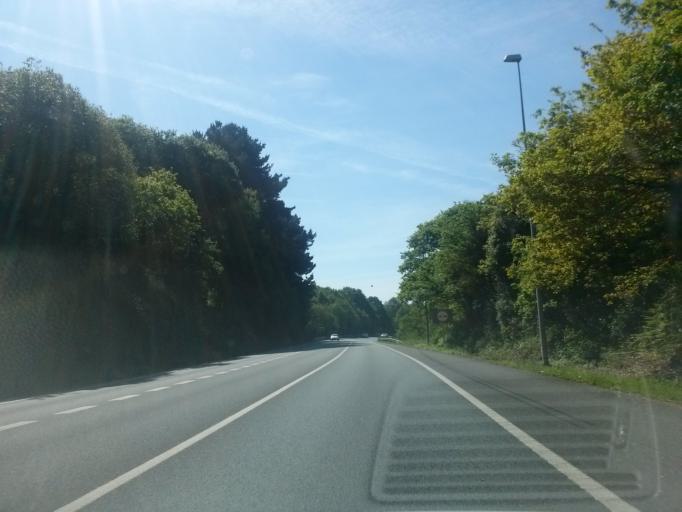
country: ES
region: Galicia
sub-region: Provincia de Lugo
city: Lugo
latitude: 43.0152
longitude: -7.5824
